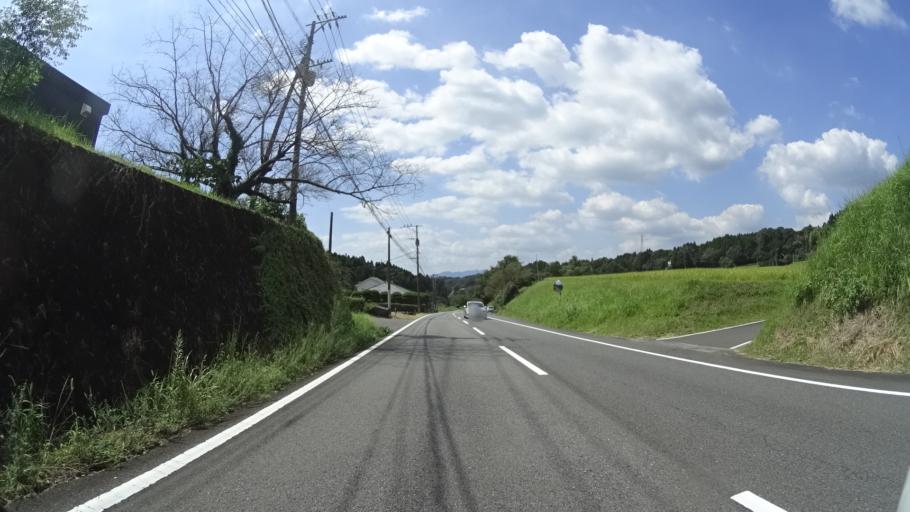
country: JP
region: Kagoshima
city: Kokubu-matsuki
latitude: 31.8612
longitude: 130.7873
